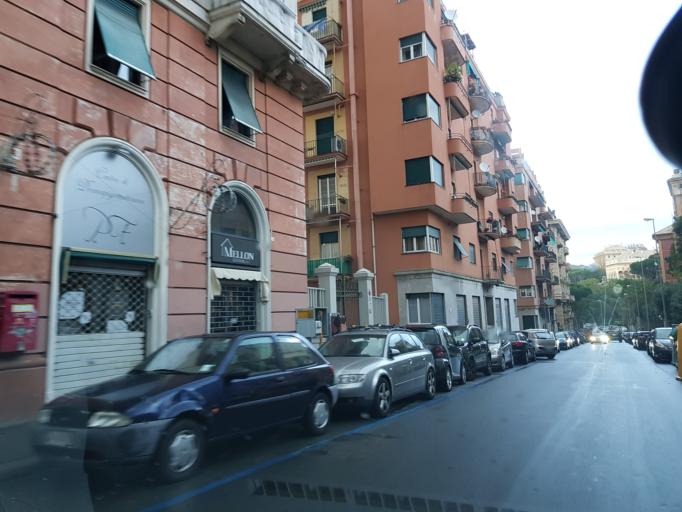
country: IT
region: Liguria
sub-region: Provincia di Genova
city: San Teodoro
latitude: 44.3989
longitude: 8.9543
